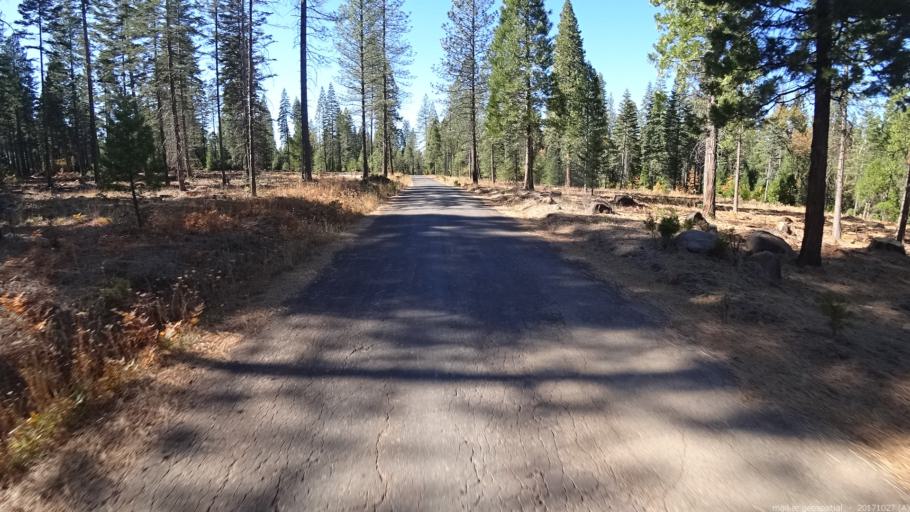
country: US
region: California
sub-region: Shasta County
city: Shingletown
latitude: 40.6225
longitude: -121.8438
